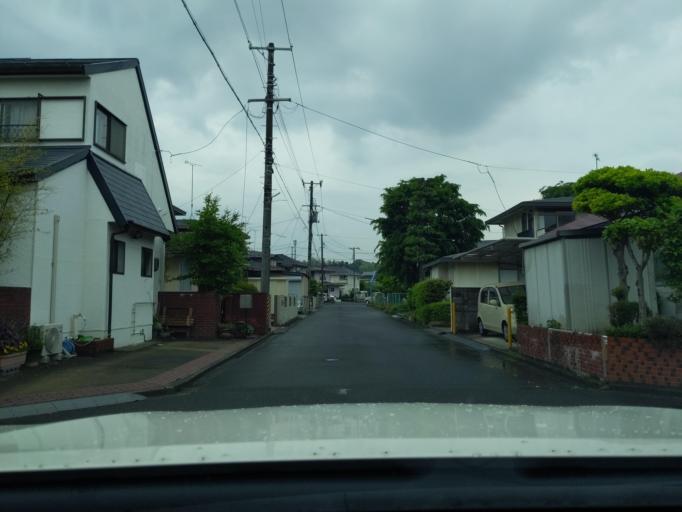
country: JP
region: Fukushima
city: Koriyama
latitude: 37.3538
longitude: 140.3575
